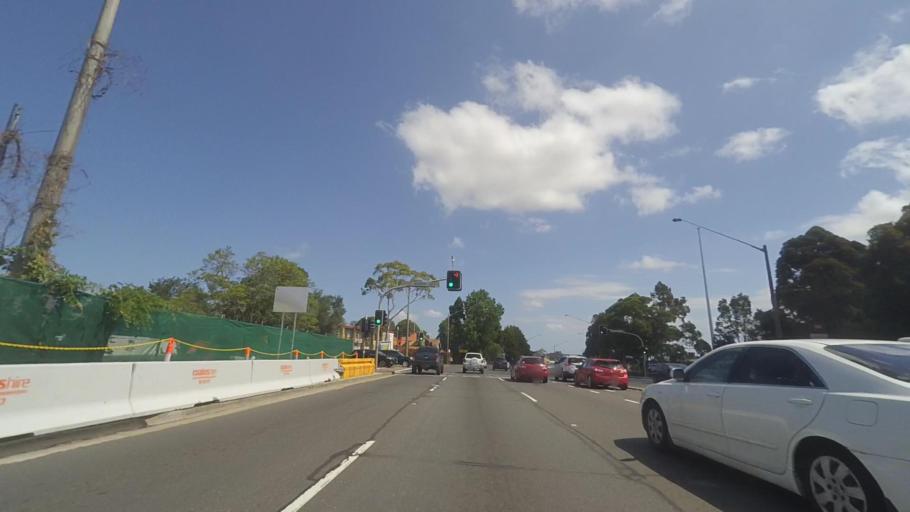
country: AU
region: New South Wales
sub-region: Hornsby Shire
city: Pennant Hills
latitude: -33.7277
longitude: 151.0841
